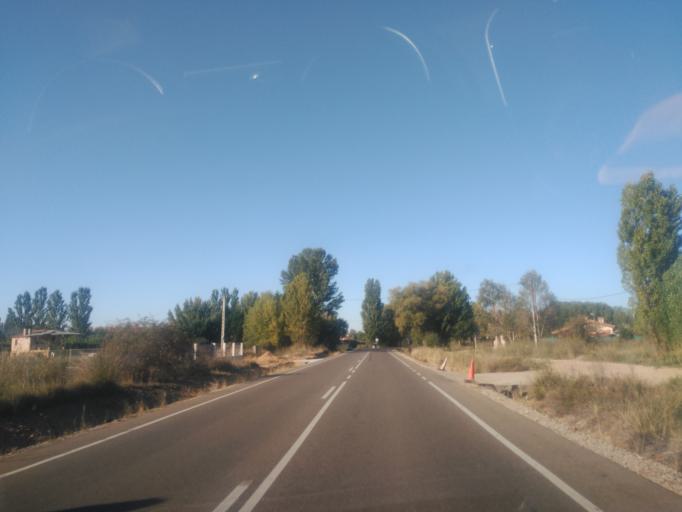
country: ES
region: Castille and Leon
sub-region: Provincia de Burgos
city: Fresnillo de las Duenas
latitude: 41.6778
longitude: -3.6441
